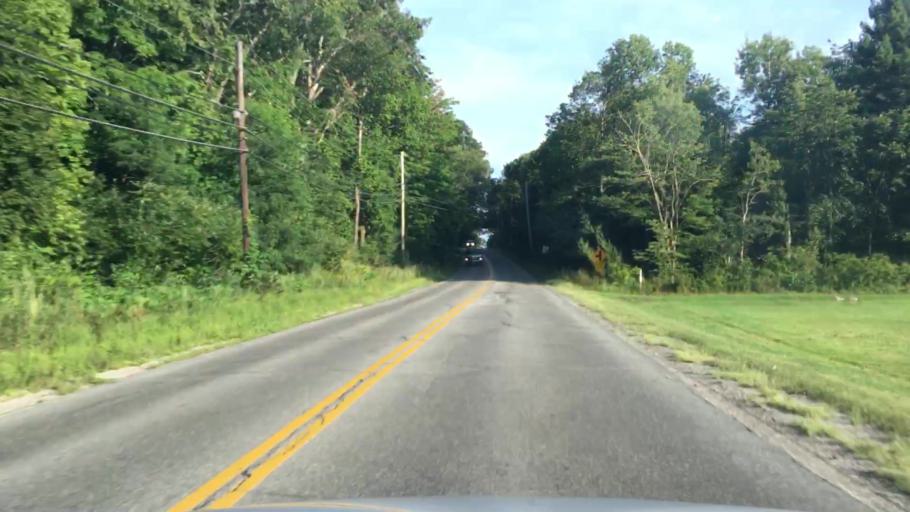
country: US
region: Maine
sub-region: Cumberland County
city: South Windham
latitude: 43.7176
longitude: -70.3943
